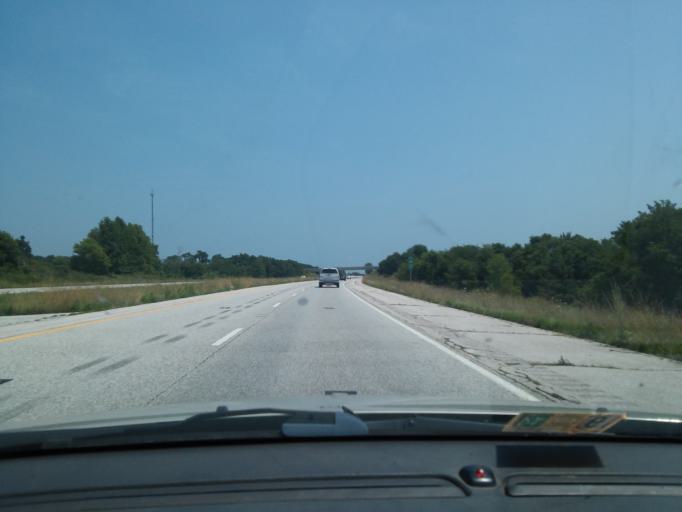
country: US
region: Illinois
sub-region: Pike County
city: Griggsville
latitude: 39.6809
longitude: -90.6772
